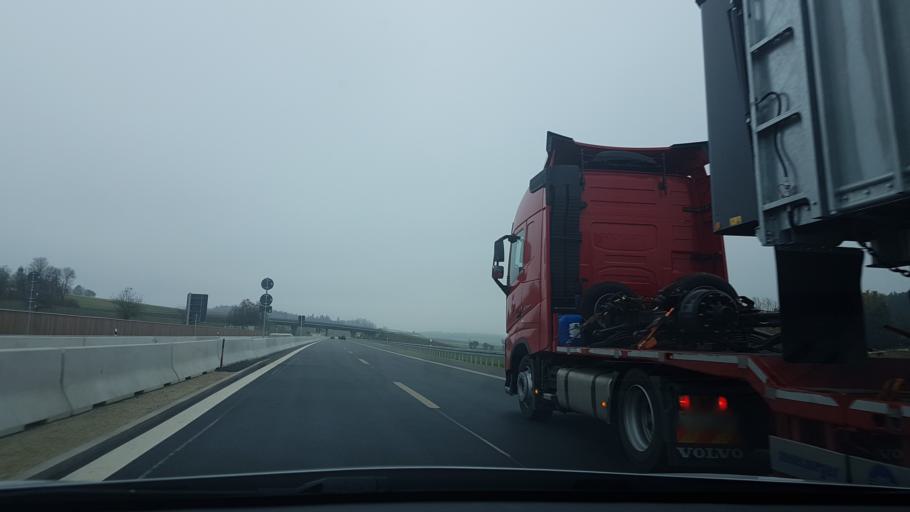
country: DE
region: Bavaria
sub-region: Lower Bavaria
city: Essenbach
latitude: 48.6230
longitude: 12.2227
